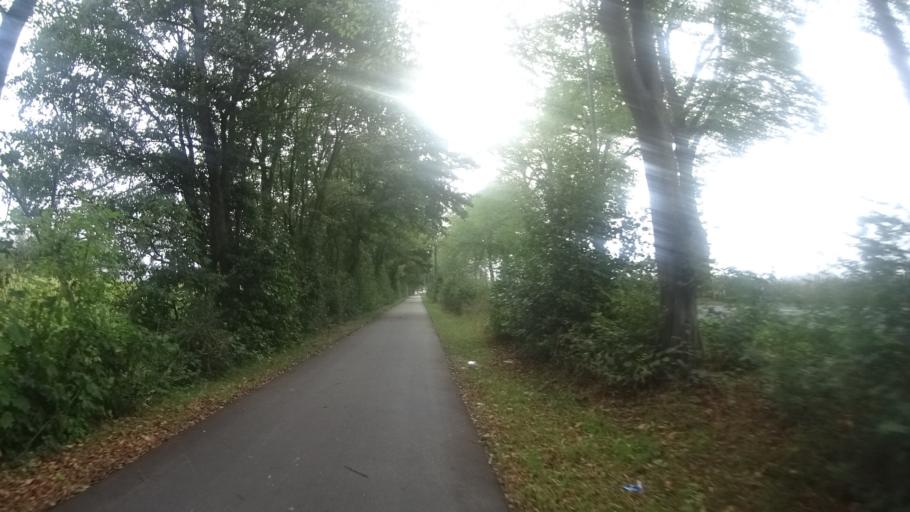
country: DE
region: North Rhine-Westphalia
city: Geldern
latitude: 51.5190
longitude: 6.3018
